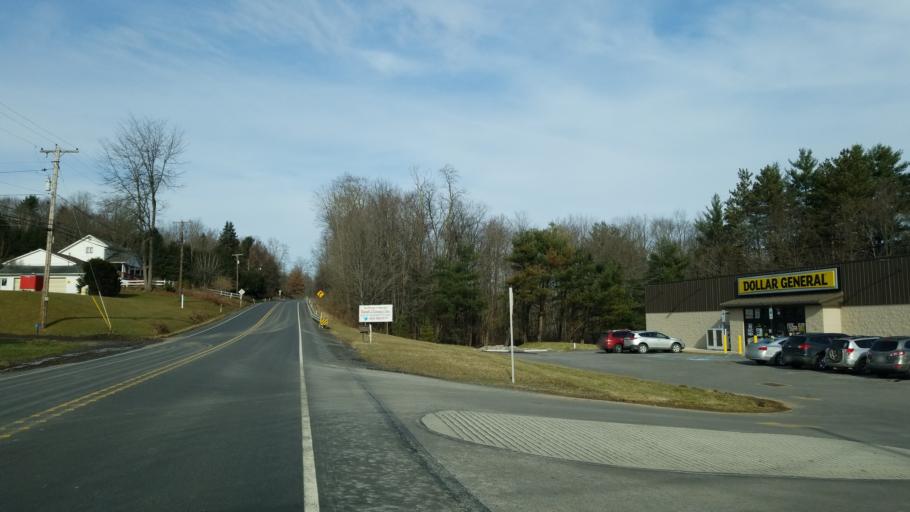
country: US
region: Pennsylvania
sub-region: Clearfield County
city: Curwensville
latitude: 40.9580
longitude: -78.6118
